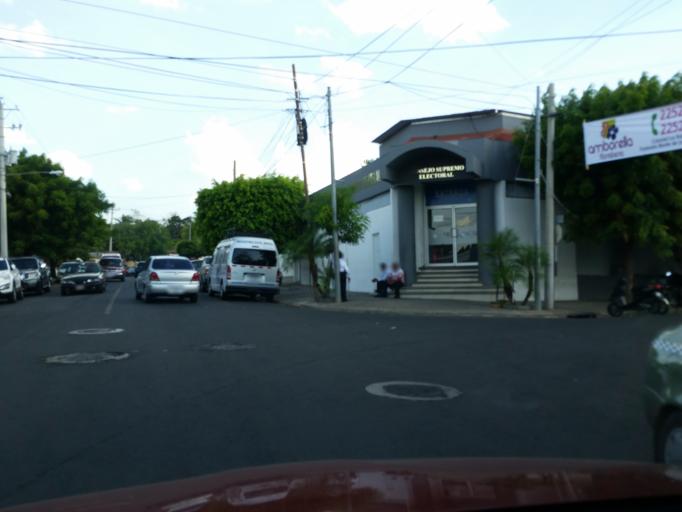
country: NI
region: Managua
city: Managua
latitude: 12.1248
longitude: -86.2581
